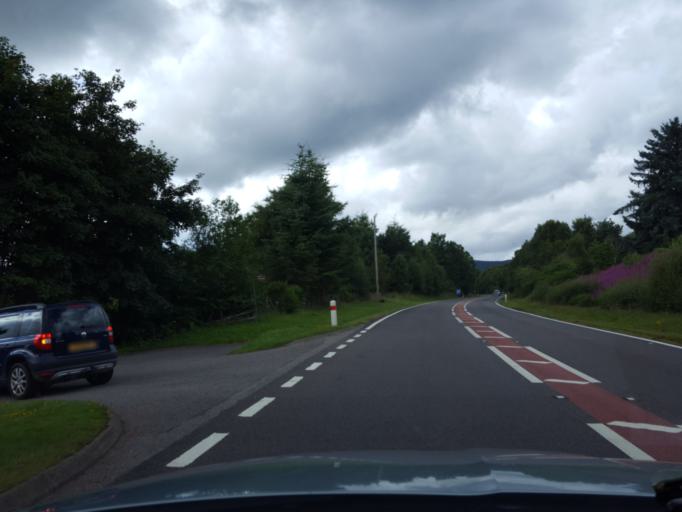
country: GB
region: Scotland
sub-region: Highland
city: Aviemore
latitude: 57.2606
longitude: -3.7435
